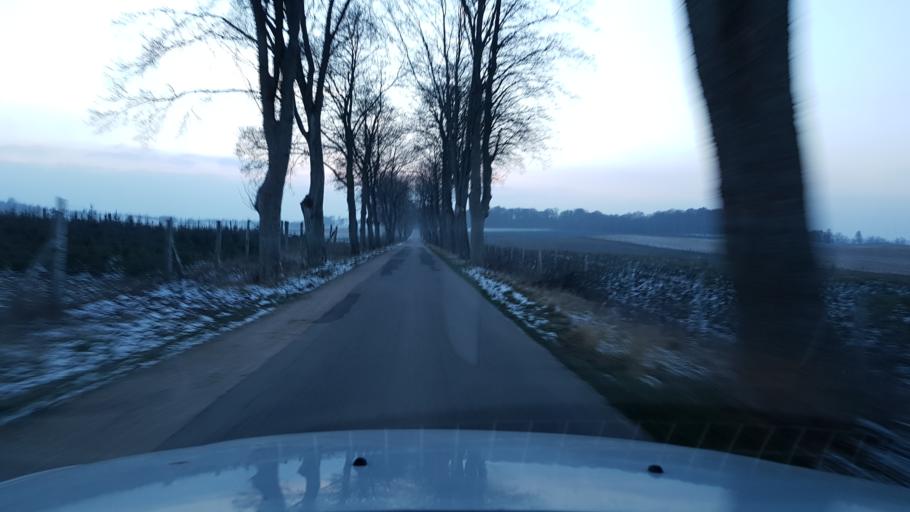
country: PL
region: West Pomeranian Voivodeship
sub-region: Powiat swidwinski
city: Slawoborze
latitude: 53.9746
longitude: 15.7799
